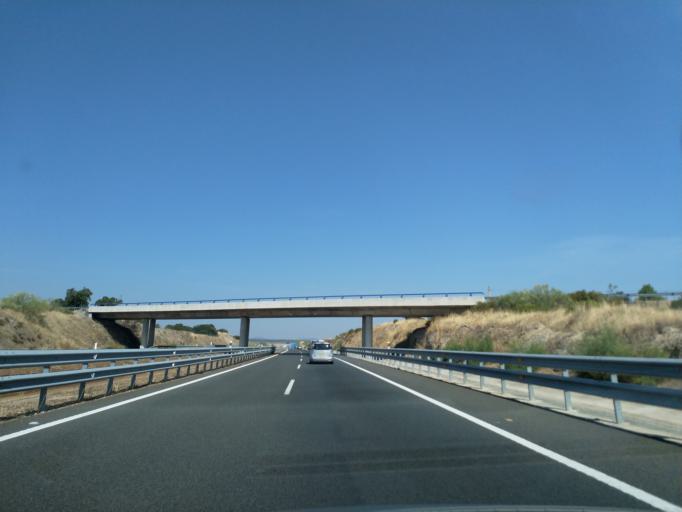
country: ES
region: Extremadura
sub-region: Provincia de Badajoz
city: Aljucen
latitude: 39.0190
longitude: -6.3306
